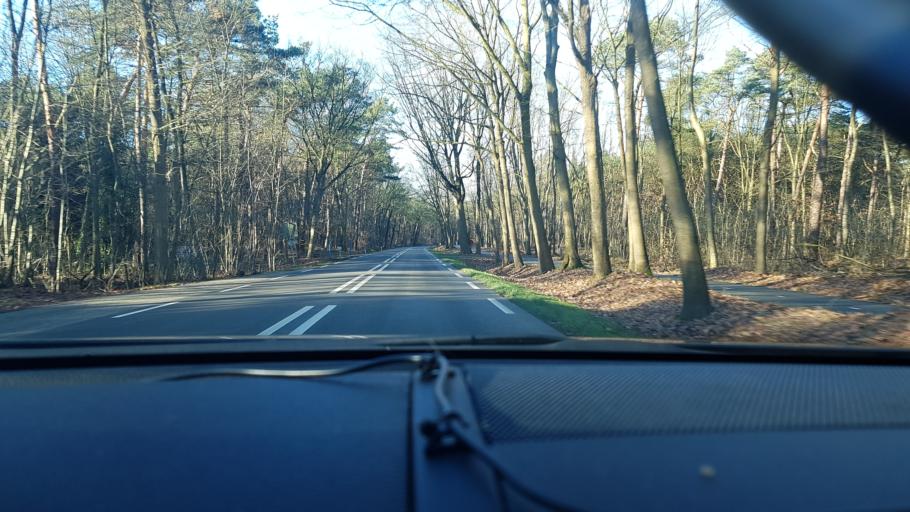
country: NL
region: Limburg
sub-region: Gemeente Beesel
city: Beesel
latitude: 51.3115
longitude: 6.0137
